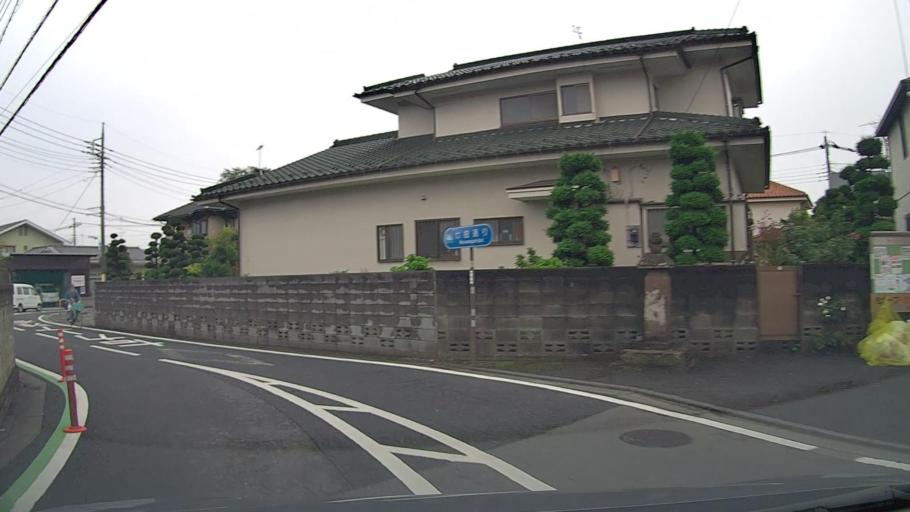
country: JP
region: Saitama
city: Tokorozawa
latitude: 35.7832
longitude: 139.4914
